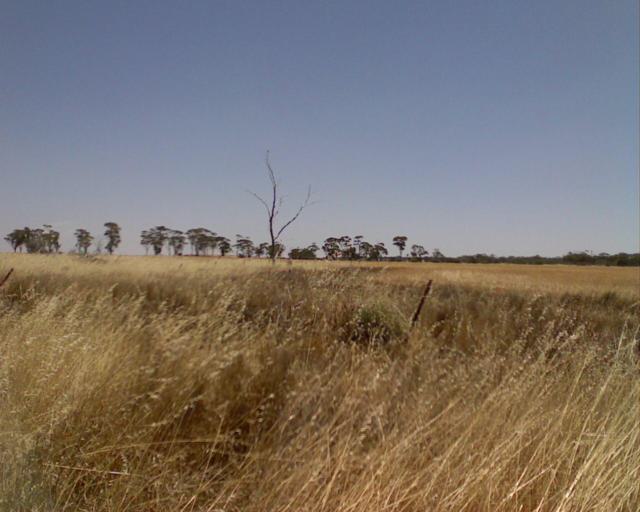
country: AU
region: Western Australia
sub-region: Wongan-Ballidu
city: Wongan Hills
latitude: -30.4549
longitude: 117.5285
